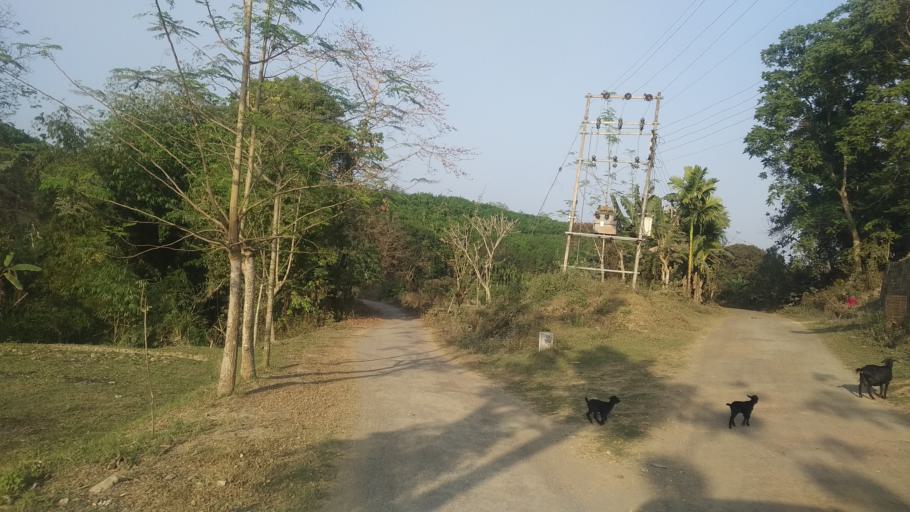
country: IN
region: Tripura
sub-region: West Tripura
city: Sonamura
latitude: 23.4421
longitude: 91.3636
